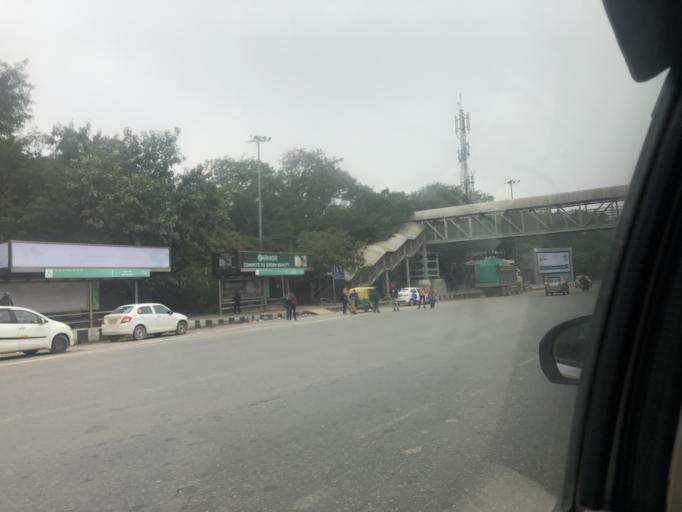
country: IN
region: NCT
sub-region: Central Delhi
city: Karol Bagh
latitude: 28.5749
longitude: 77.1478
